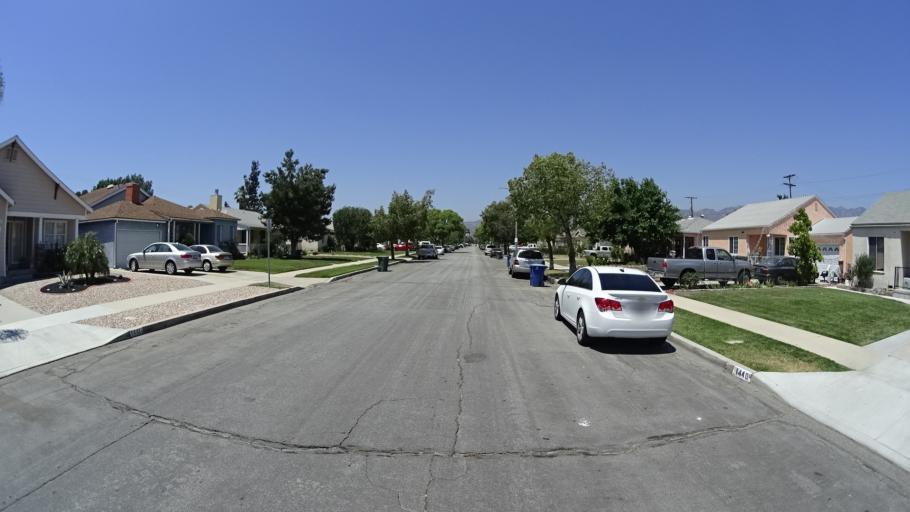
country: US
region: California
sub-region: Los Angeles County
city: Burbank
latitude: 34.1824
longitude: -118.3406
